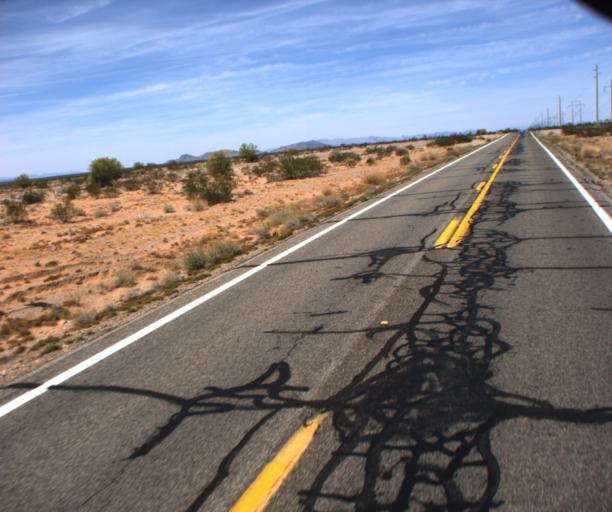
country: US
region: Arizona
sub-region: La Paz County
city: Quartzsite
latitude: 33.8294
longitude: -114.2170
